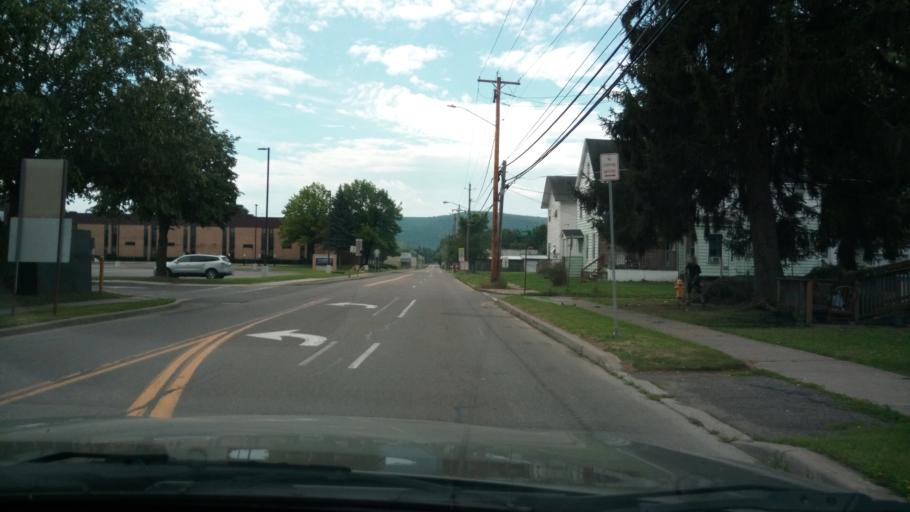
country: US
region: New York
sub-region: Chemung County
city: Elmira
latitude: 42.0698
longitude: -76.7986
